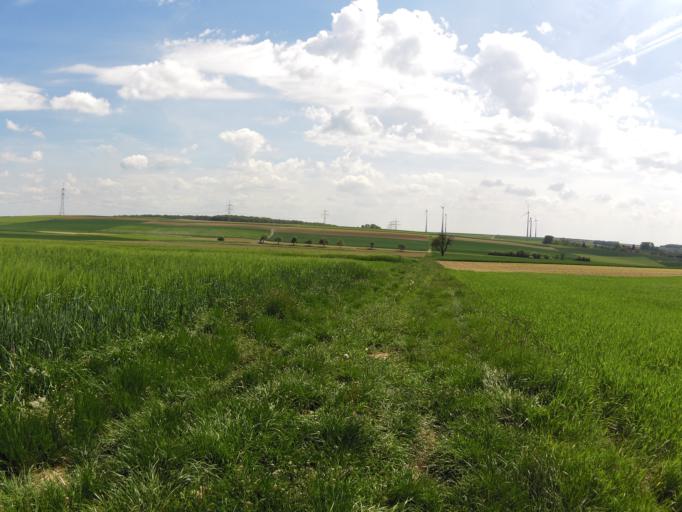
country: DE
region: Bavaria
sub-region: Regierungsbezirk Unterfranken
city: Theilheim
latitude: 49.7426
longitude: 10.0370
